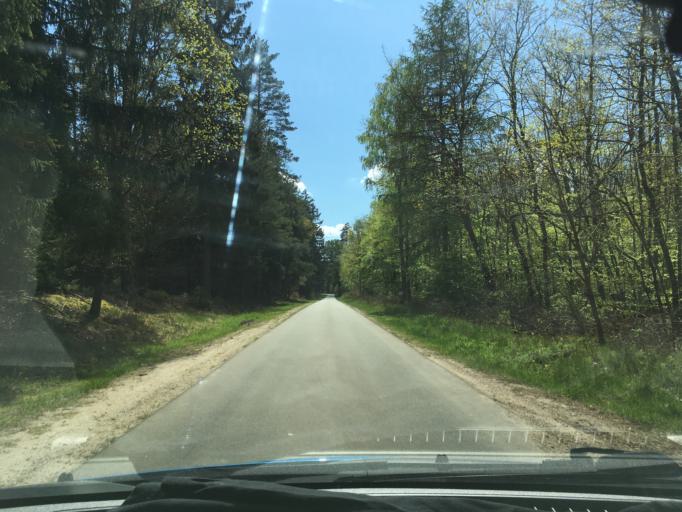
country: DE
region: Lower Saxony
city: Stoetze
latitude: 53.1089
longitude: 10.7851
